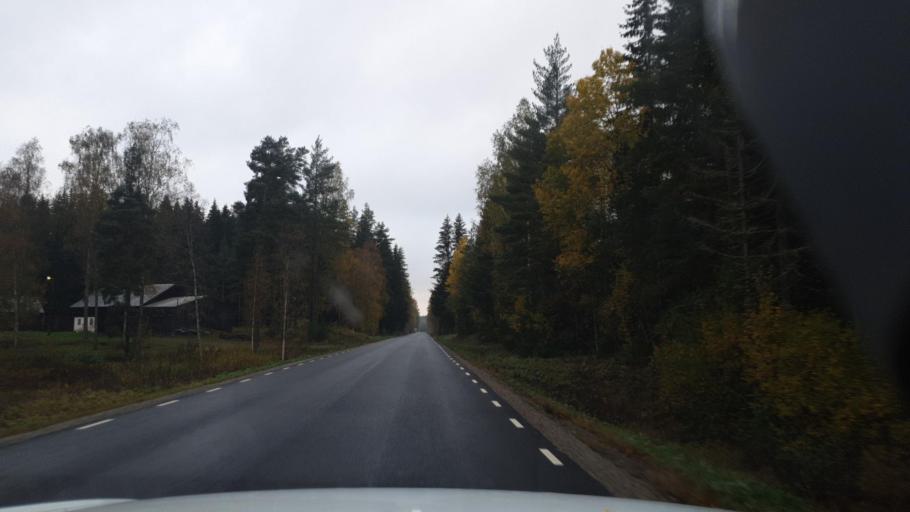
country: SE
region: Vaermland
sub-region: Arvika Kommun
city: Arvika
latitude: 59.6530
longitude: 12.7328
